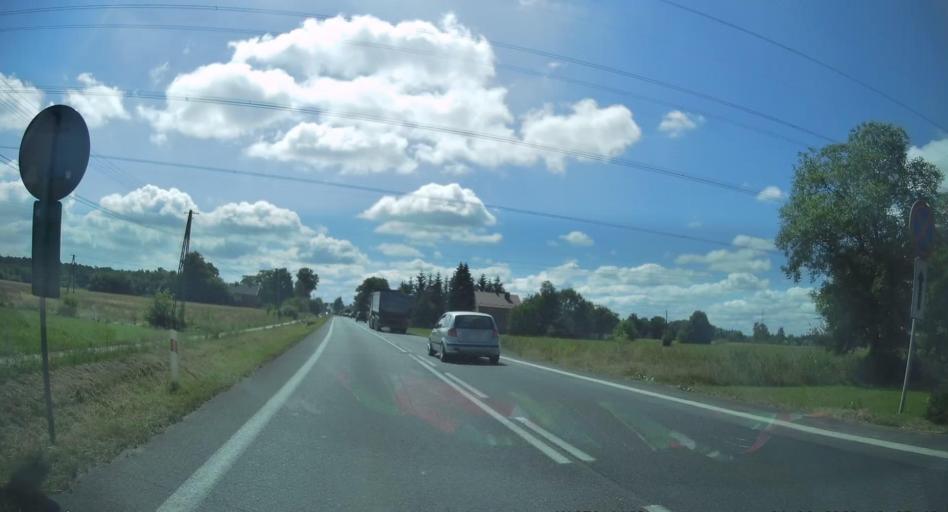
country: PL
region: Subcarpathian Voivodeship
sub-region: Powiat debicki
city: Brzeznica
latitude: 50.1274
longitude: 21.4854
